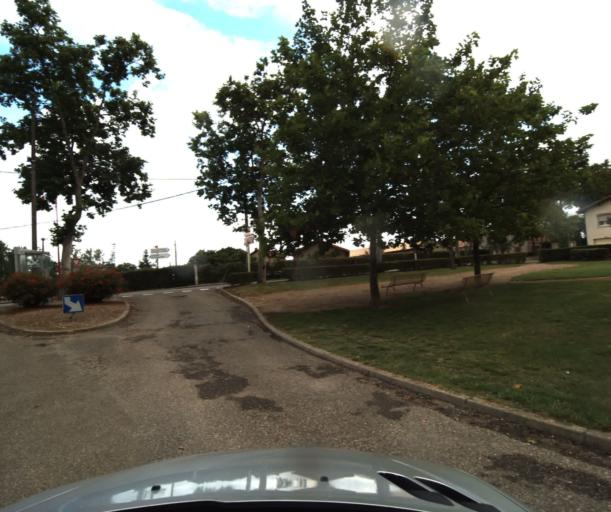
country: FR
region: Midi-Pyrenees
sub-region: Departement du Tarn-et-Garonne
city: Lavit
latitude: 43.9598
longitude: 0.9252
